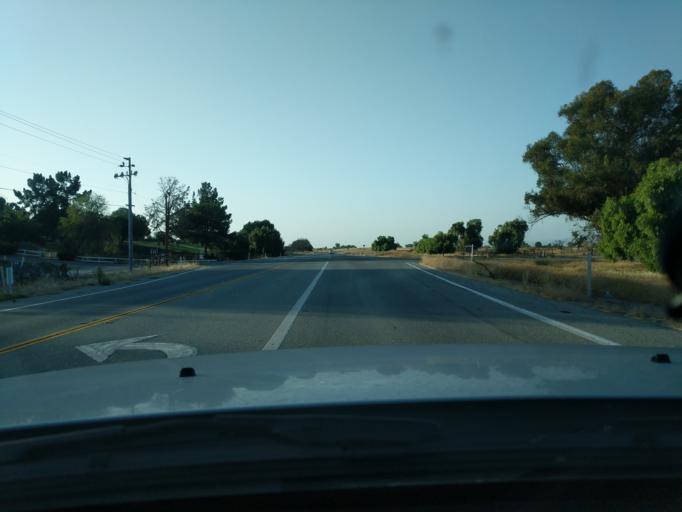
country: US
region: California
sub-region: San Benito County
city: Ridgemark
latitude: 36.8087
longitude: -121.3453
